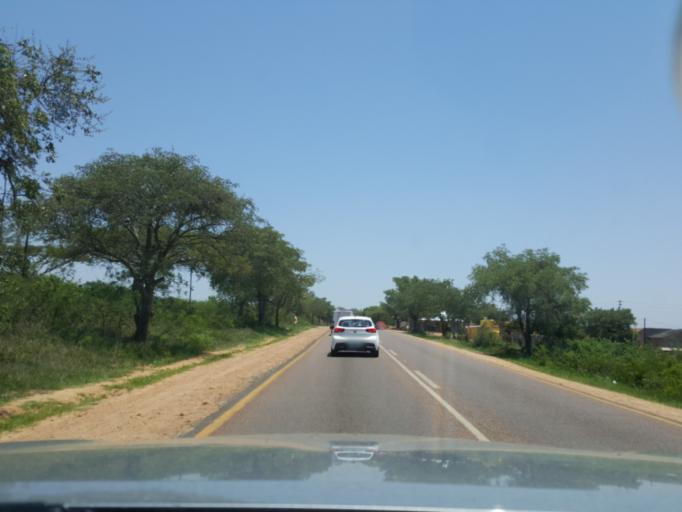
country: ZA
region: Limpopo
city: Thulamahashi
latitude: -24.6372
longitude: 31.0420
